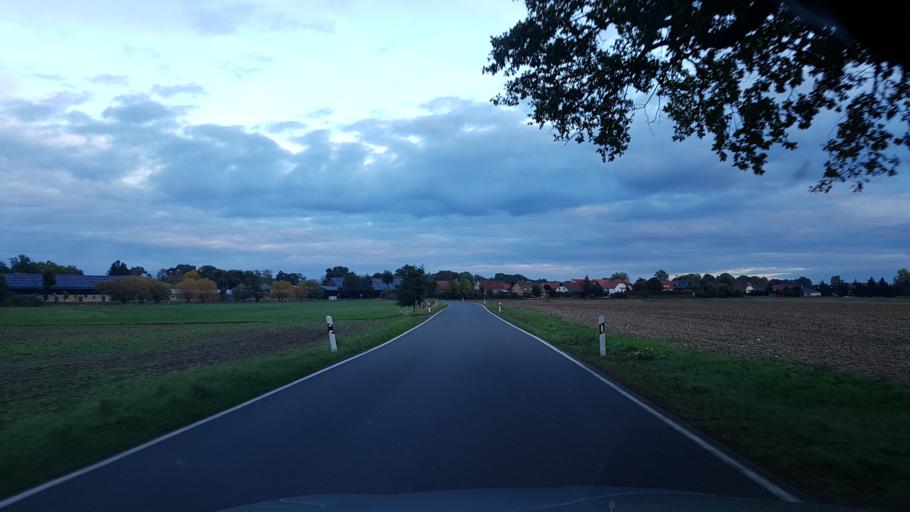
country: DE
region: Saxony
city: Ebersbach
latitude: 51.2791
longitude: 13.6183
